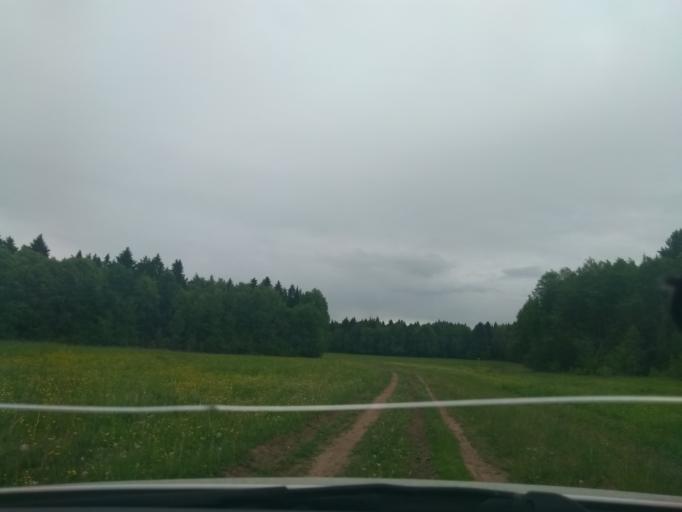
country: RU
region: Perm
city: Perm
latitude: 57.9844
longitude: 56.3308
